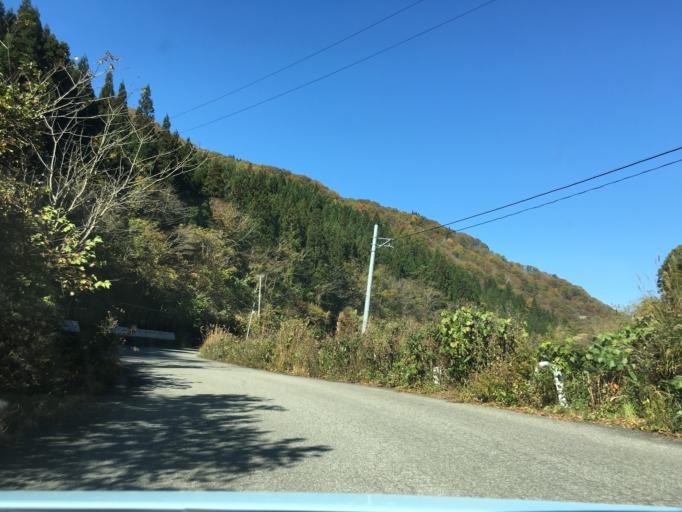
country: JP
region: Fukushima
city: Inawashiro
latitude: 37.4168
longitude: 139.9893
